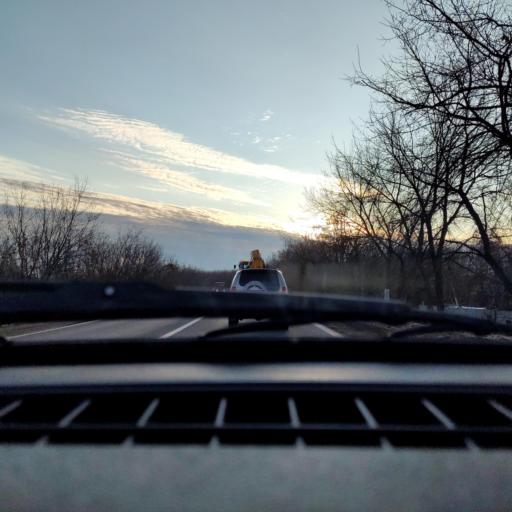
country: RU
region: Bashkortostan
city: Iglino
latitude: 54.7755
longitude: 56.2402
